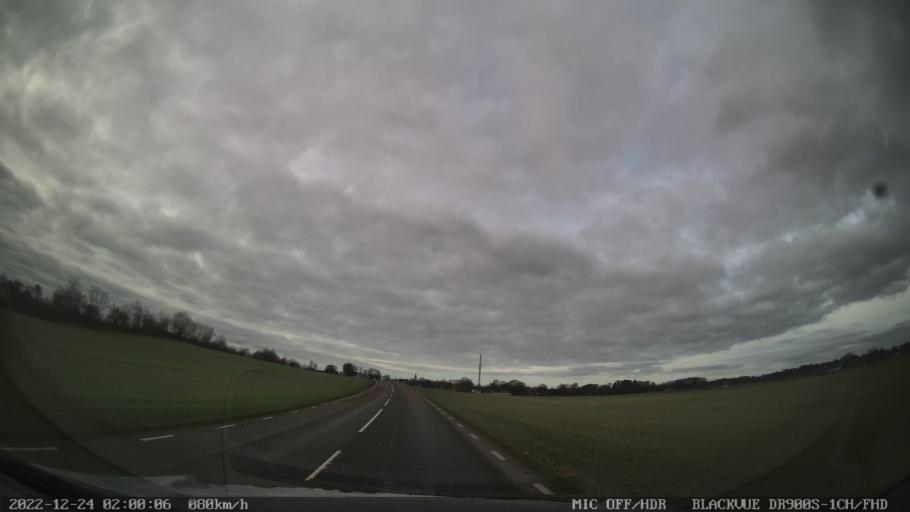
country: SE
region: Skane
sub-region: Tomelilla Kommun
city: Tomelilla
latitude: 55.6114
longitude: 14.0038
